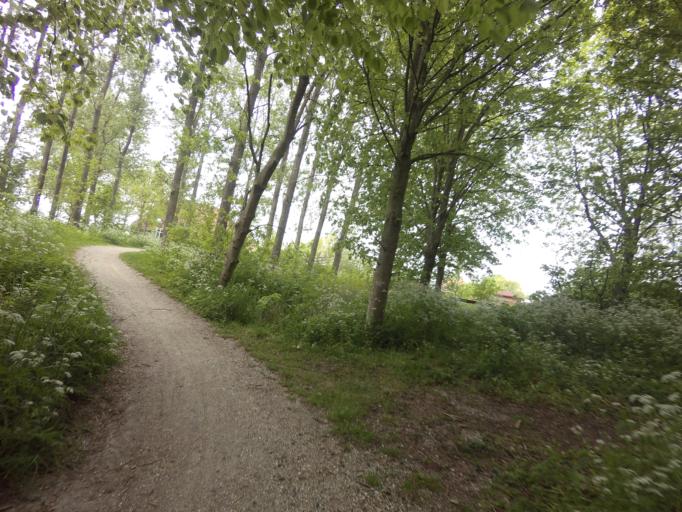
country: NL
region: Friesland
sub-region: Sudwest Fryslan
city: Bolsward
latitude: 53.0966
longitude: 5.4729
